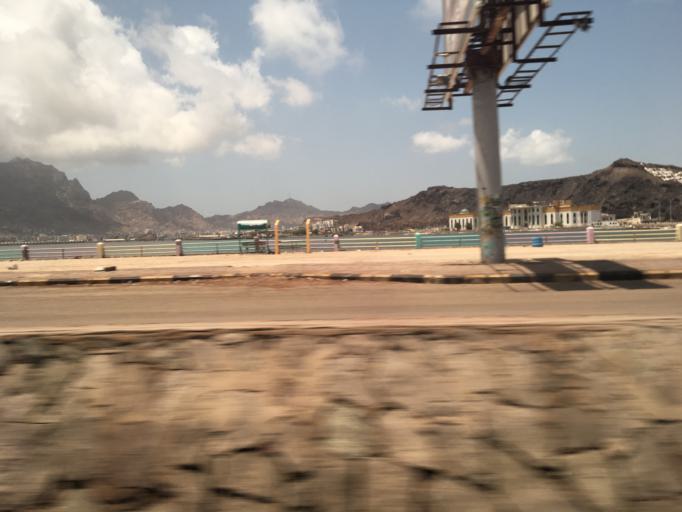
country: YE
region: Aden
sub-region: Khur Maksar
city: Khawr Maksar
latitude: 12.8101
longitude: 45.0245
